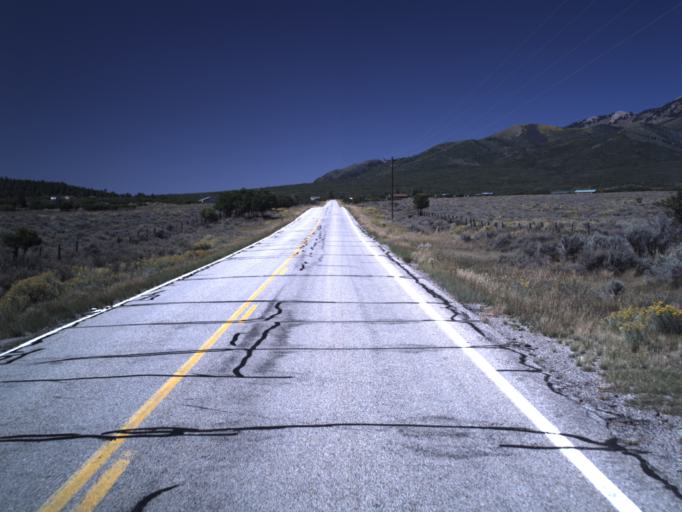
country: US
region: Utah
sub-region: Grand County
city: Moab
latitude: 38.3411
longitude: -109.1724
